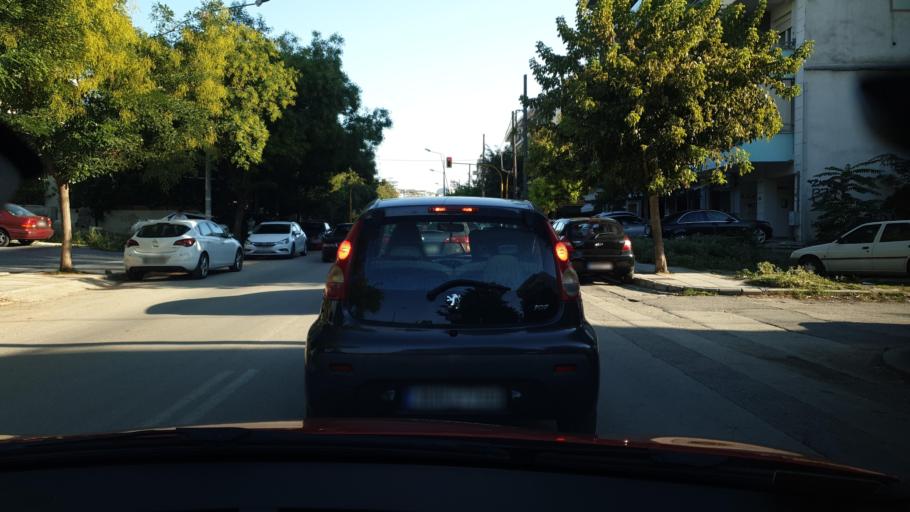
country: GR
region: Central Macedonia
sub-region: Nomos Thessalonikis
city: Triandria
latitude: 40.6032
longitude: 22.9746
